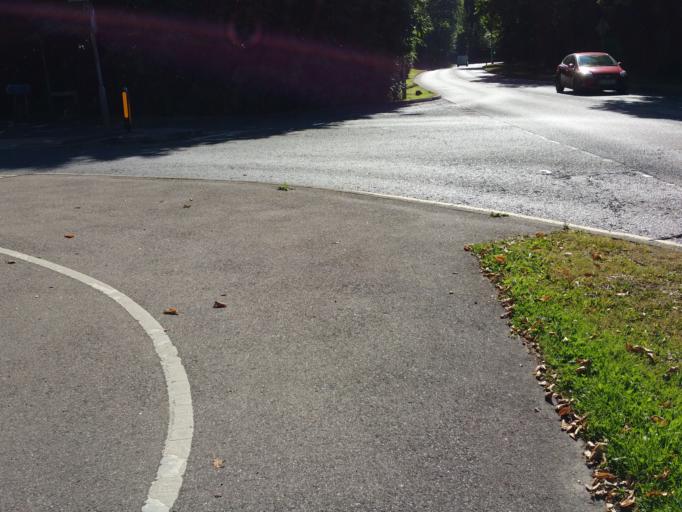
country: GB
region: England
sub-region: Kent
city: Boxley
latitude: 51.3360
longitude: 0.5461
